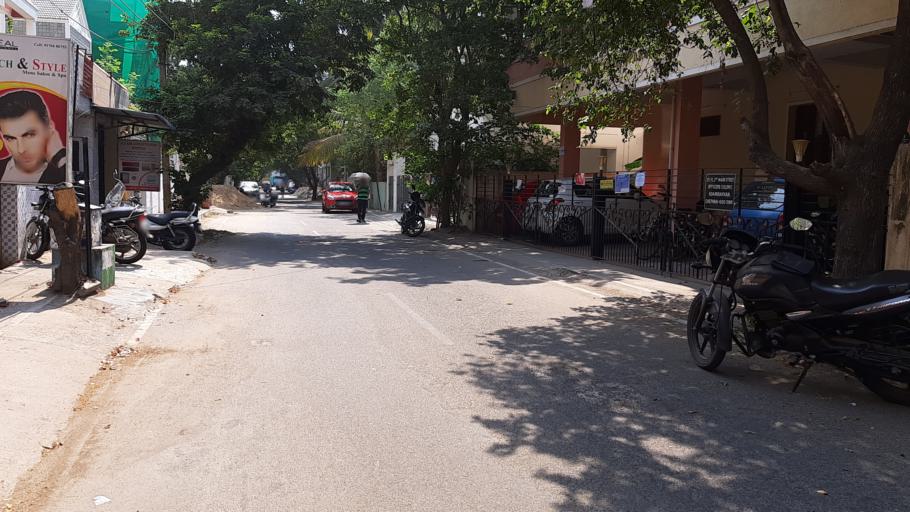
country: IN
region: Tamil Nadu
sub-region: Kancheepuram
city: Alandur
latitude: 12.9955
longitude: 80.2063
